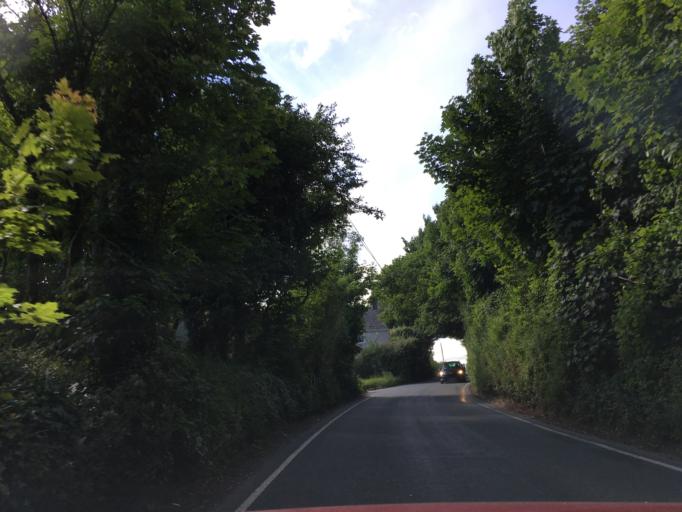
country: GB
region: England
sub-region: Devon
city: Dartmouth
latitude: 50.3487
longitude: -3.6160
